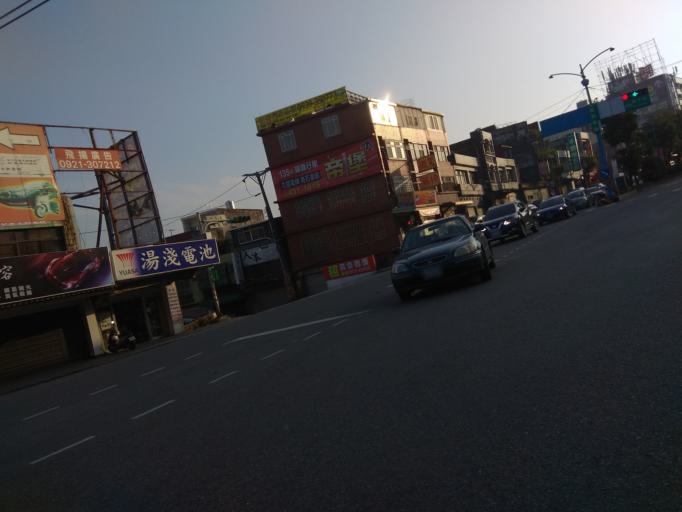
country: TW
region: Taiwan
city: Daxi
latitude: 24.9237
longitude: 121.1876
